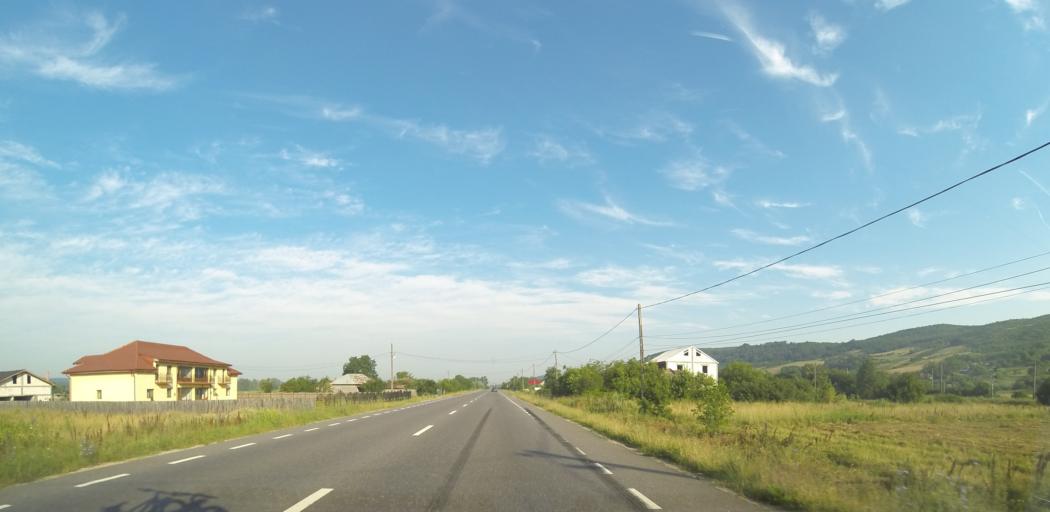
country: RO
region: Mehedinti
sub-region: Comuna Butoiesti
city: Butoiesti
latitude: 44.5863
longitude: 23.3489
